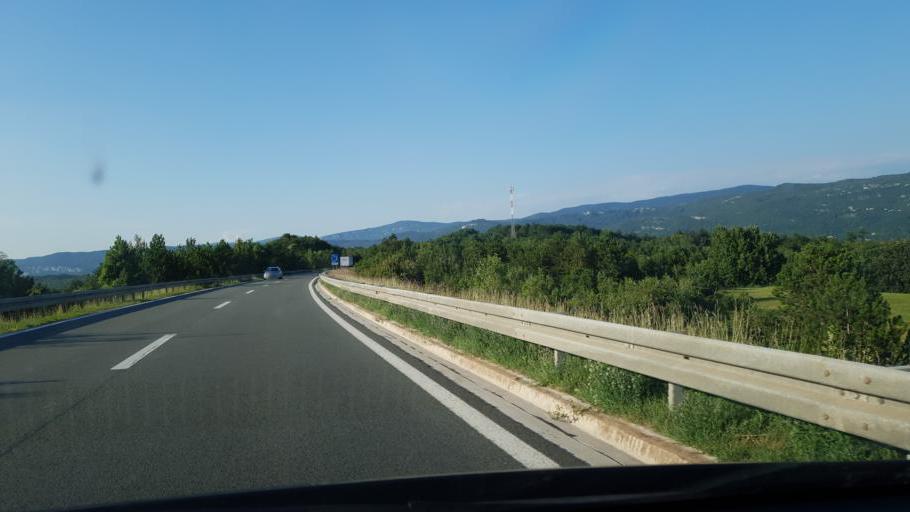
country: HR
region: Istarska
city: Buzet
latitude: 45.3303
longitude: 14.0740
